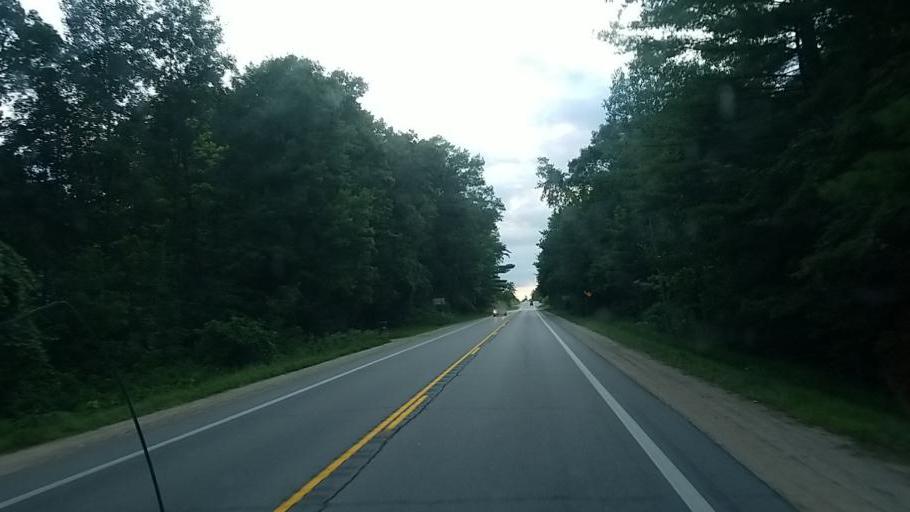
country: US
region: Michigan
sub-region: Newaygo County
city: Newaygo
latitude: 43.4237
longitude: -85.8174
